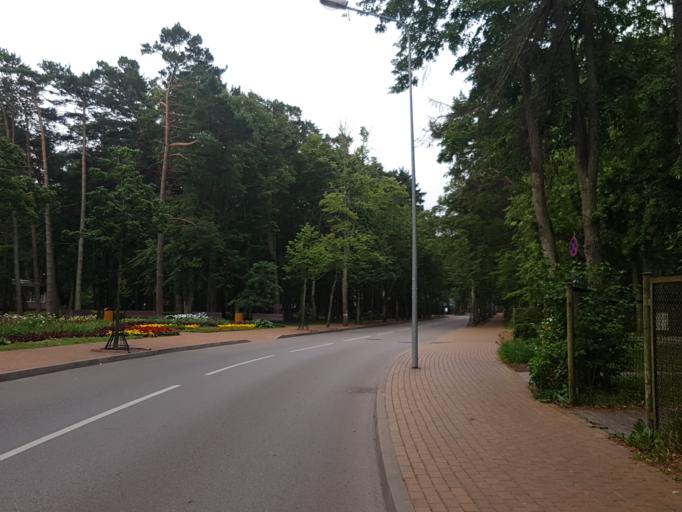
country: LT
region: Klaipedos apskritis
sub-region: Klaipeda
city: Palanga
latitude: 55.9173
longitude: 21.0581
